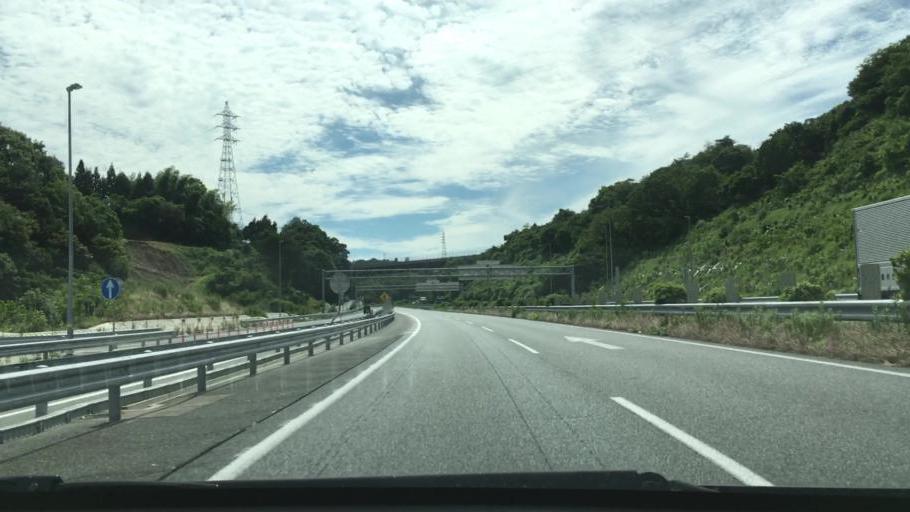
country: JP
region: Yamaguchi
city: Ogori-shimogo
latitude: 34.1265
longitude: 131.4003
